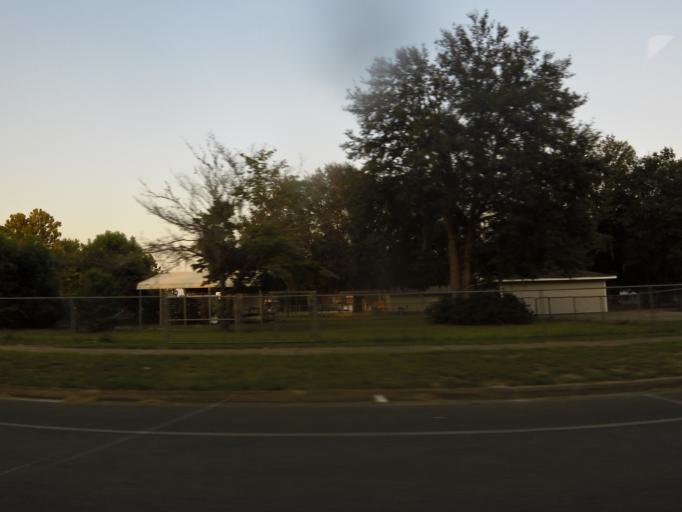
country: US
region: Florida
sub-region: Baker County
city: Macclenny
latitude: 30.2844
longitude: -82.1227
